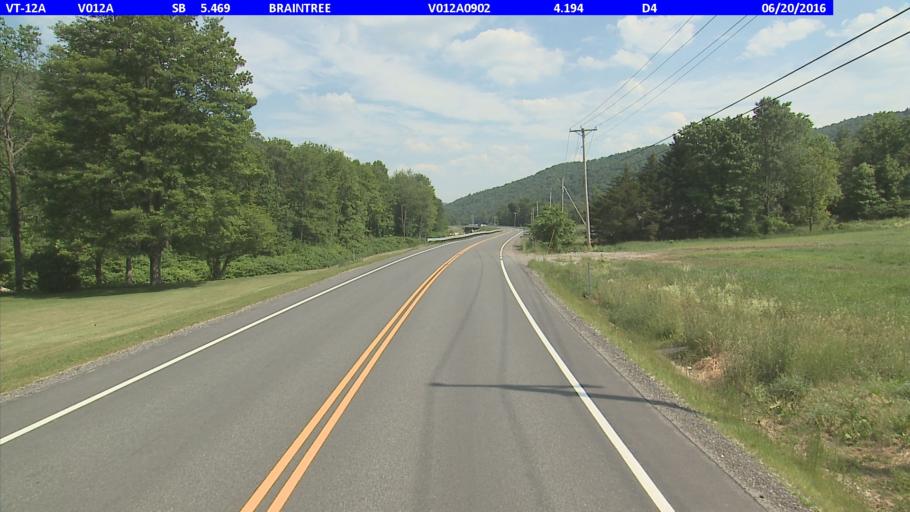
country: US
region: Vermont
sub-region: Orange County
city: Randolph
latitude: 43.9687
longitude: -72.7454
